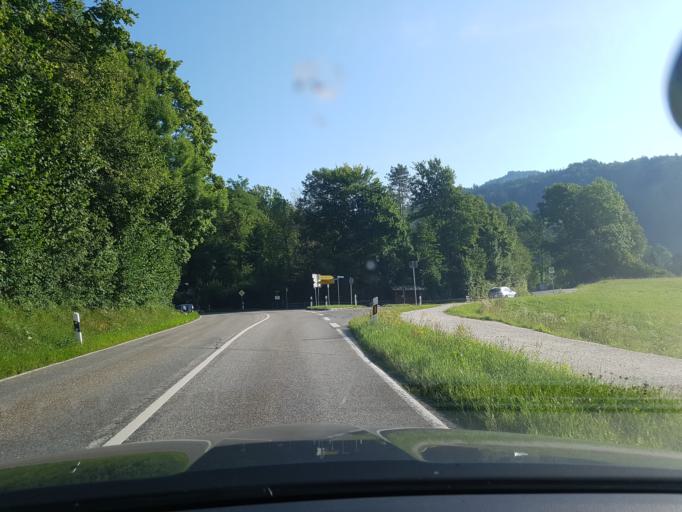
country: DE
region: Bavaria
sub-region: Upper Bavaria
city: Berchtesgaden
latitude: 47.6437
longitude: 13.0001
